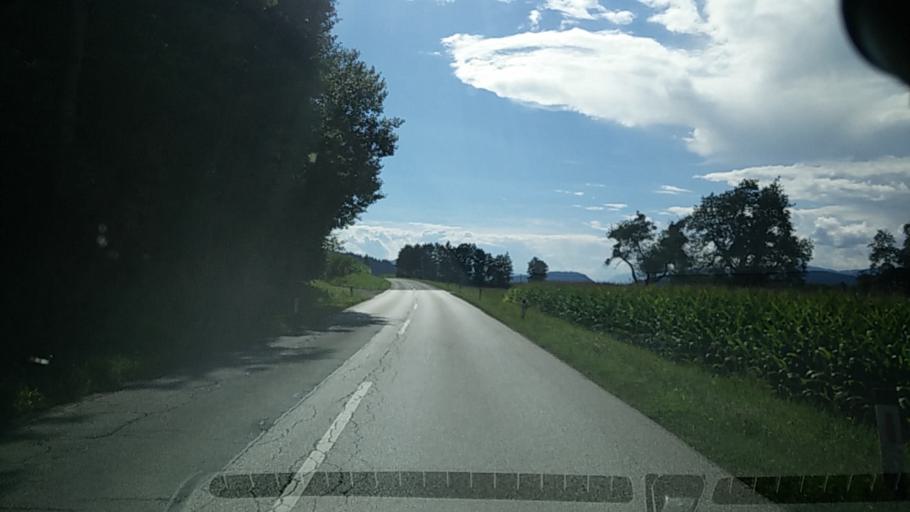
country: AT
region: Carinthia
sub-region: Politischer Bezirk Sankt Veit an der Glan
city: St. Georgen am Laengsee
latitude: 46.7495
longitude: 14.4300
